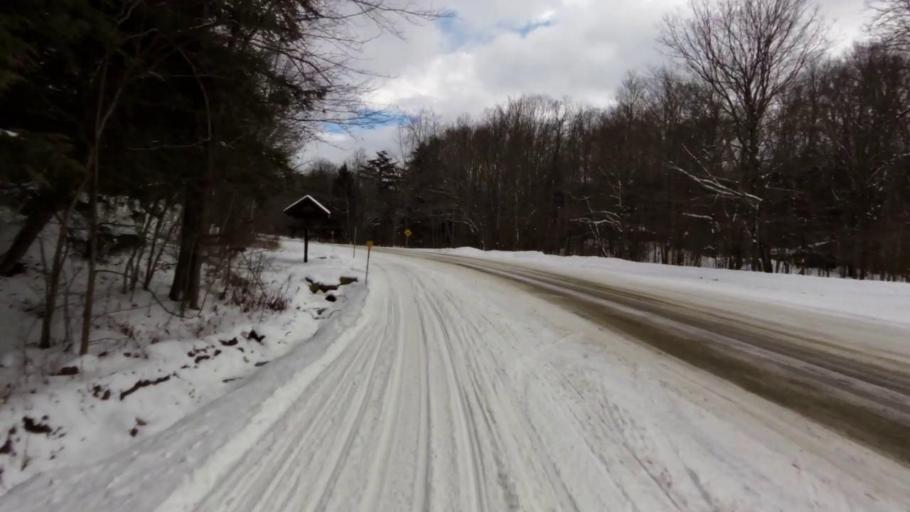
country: US
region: Pennsylvania
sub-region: McKean County
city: Bradford
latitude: 42.0092
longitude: -78.8008
